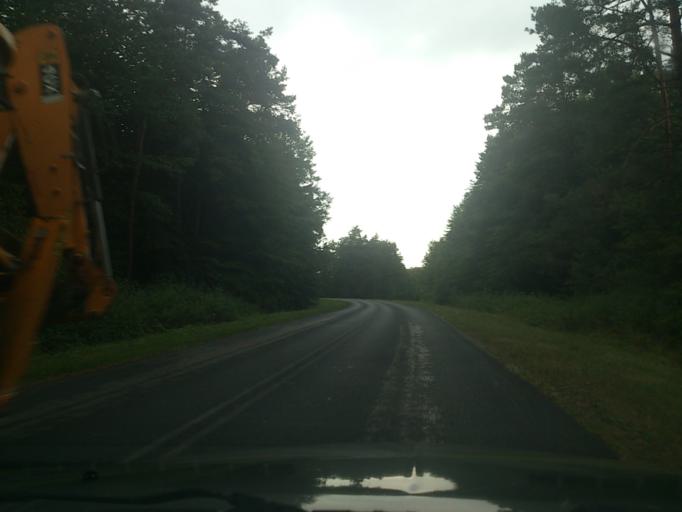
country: PL
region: Kujawsko-Pomorskie
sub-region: Powiat golubsko-dobrzynski
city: Golub-Dobrzyn
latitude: 53.0862
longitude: 19.0550
